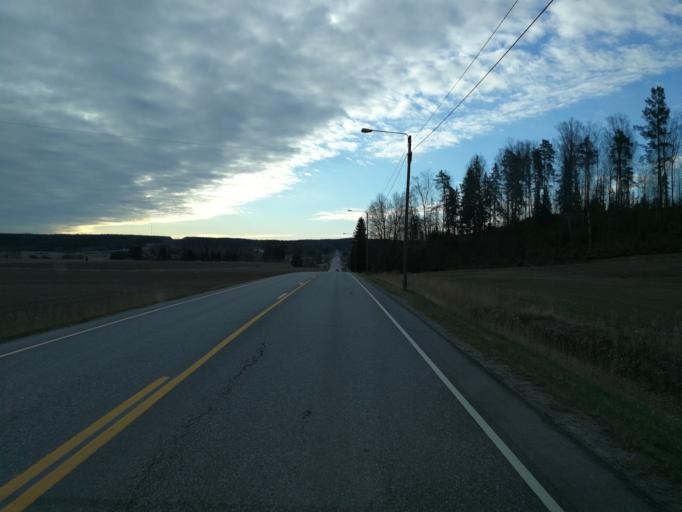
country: FI
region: Varsinais-Suomi
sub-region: Turku
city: Paimio
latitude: 60.4236
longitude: 22.6413
